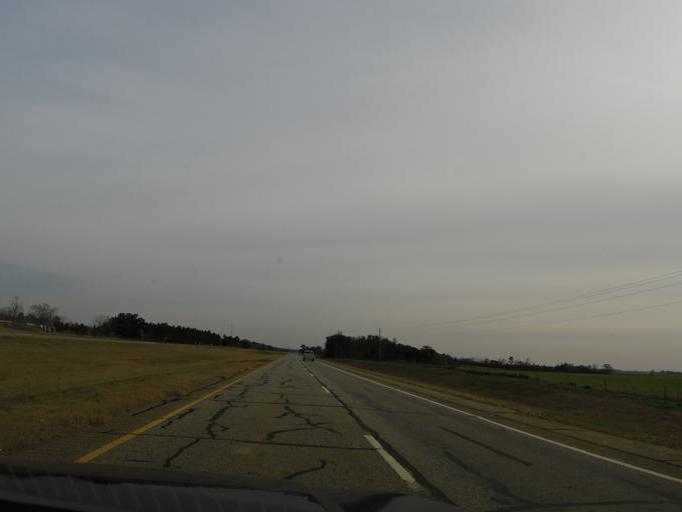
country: US
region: Georgia
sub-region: Seminole County
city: Donalsonville
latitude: 31.0606
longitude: -84.9256
